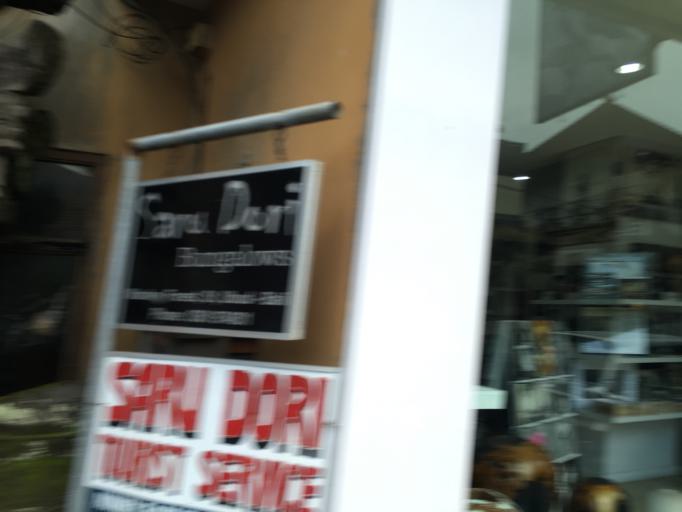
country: ID
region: Bali
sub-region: Kabupaten Gianyar
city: Ubud
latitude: -8.5092
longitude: 115.2615
